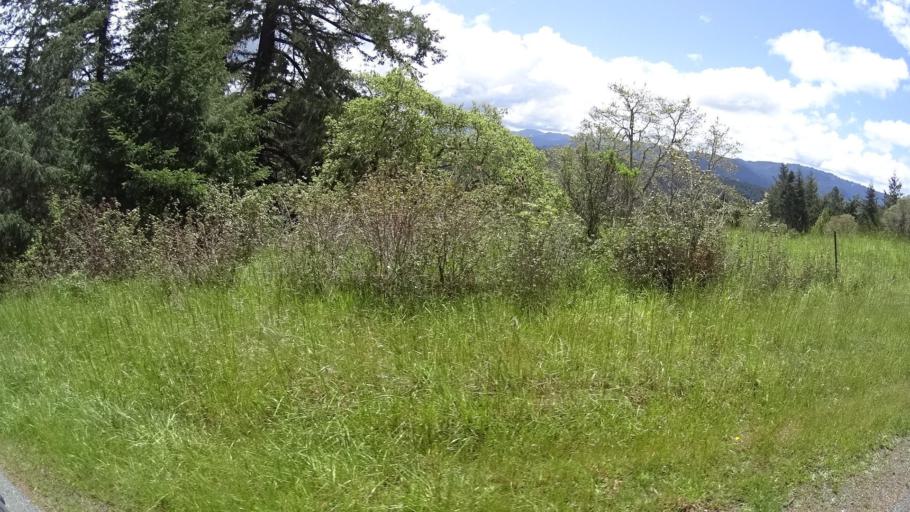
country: US
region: California
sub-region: Humboldt County
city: Blue Lake
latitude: 40.8436
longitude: -123.9033
